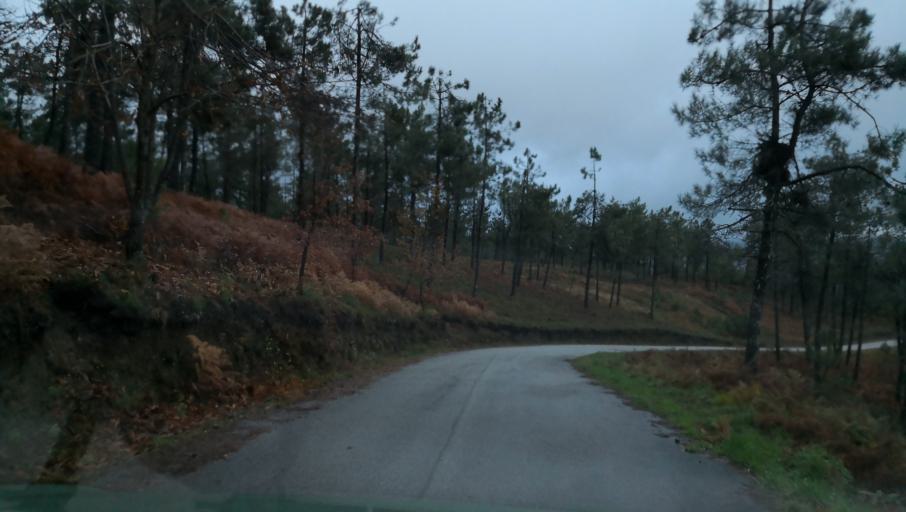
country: PT
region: Vila Real
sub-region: Santa Marta de Penaguiao
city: Santa Marta de Penaguiao
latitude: 41.2916
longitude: -7.8938
